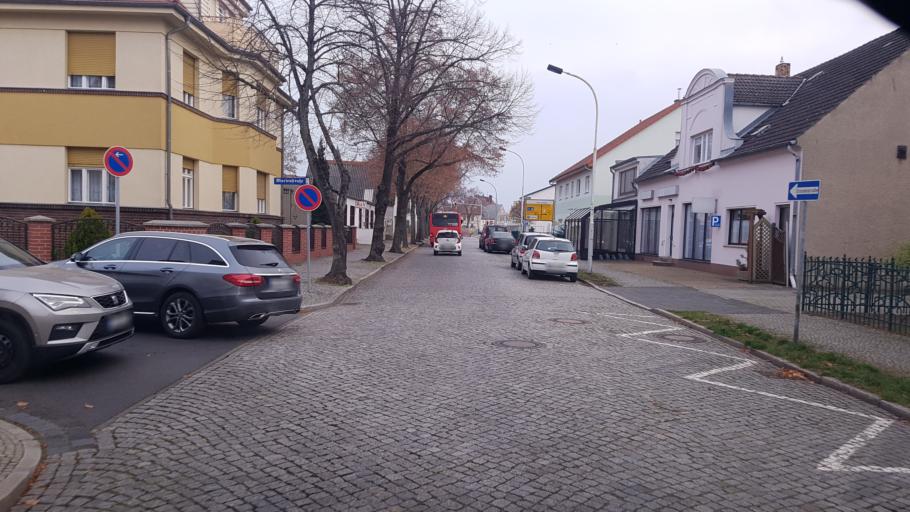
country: DE
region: Brandenburg
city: Eisenhuettenstadt
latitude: 52.1446
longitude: 14.6671
